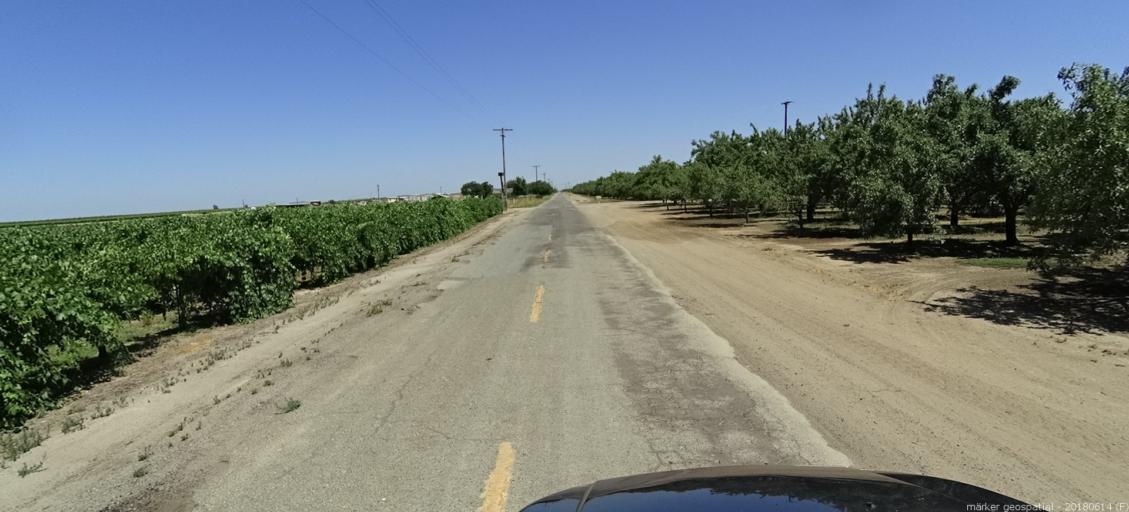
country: US
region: California
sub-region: Madera County
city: Fairmead
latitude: 37.0249
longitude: -120.2387
